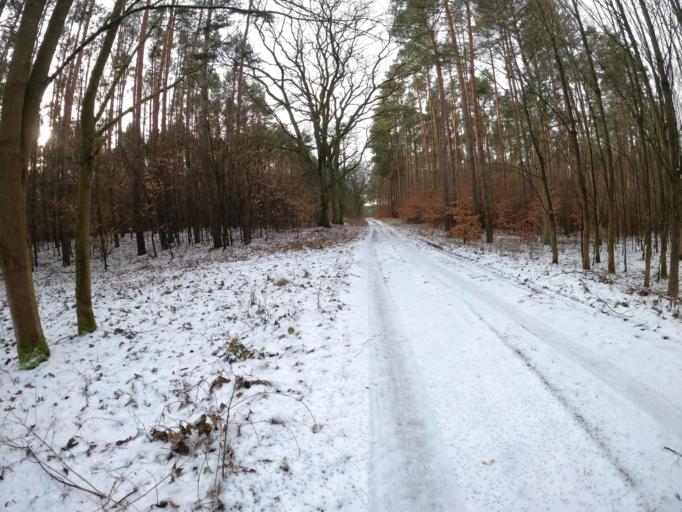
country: PL
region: Lubusz
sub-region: Powiat slubicki
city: Rzepin
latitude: 52.2866
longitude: 14.8100
